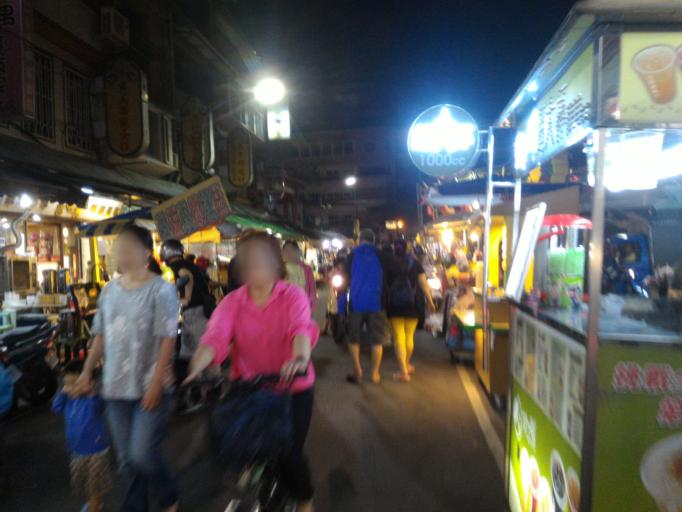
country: TW
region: Taipei
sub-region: Taipei
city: Banqiao
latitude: 25.0837
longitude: 121.4713
